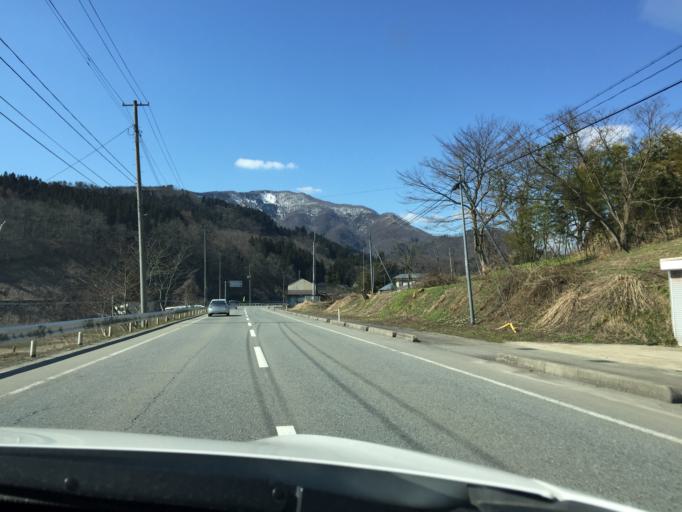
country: JP
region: Yamagata
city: Nagai
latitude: 38.2312
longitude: 140.0915
